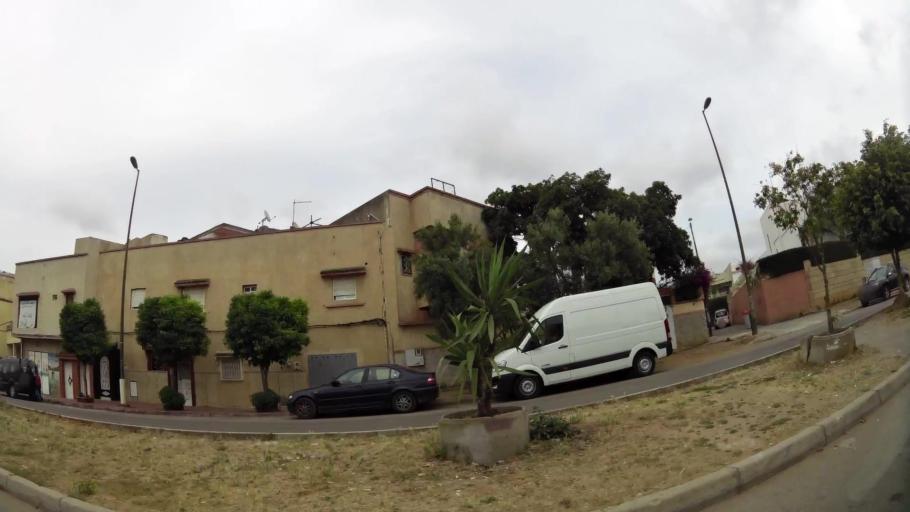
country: MA
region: Rabat-Sale-Zemmour-Zaer
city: Sale
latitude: 34.0273
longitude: -6.8063
